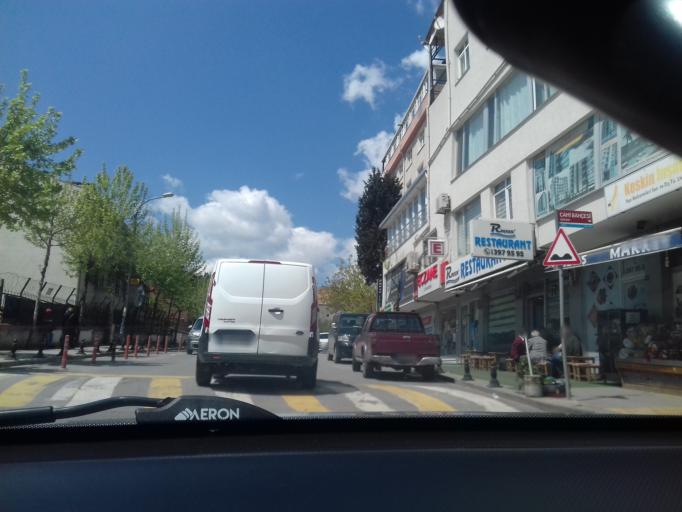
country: TR
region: Istanbul
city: Pendik
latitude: 40.8707
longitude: 29.2733
